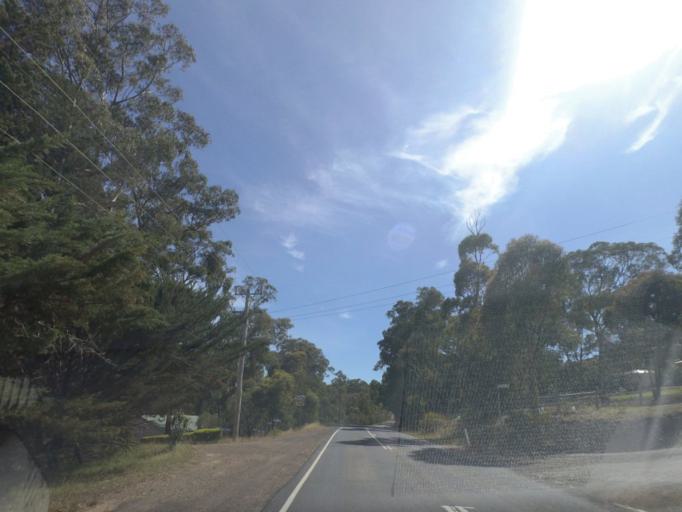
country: AU
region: Victoria
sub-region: Nillumbik
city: Saint Andrews
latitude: -37.5986
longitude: 145.2765
